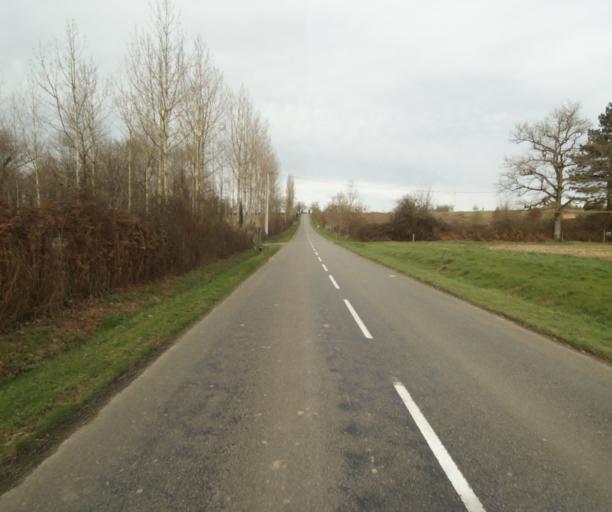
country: FR
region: Aquitaine
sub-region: Departement des Landes
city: Gabarret
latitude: 43.9607
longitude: 0.0059
